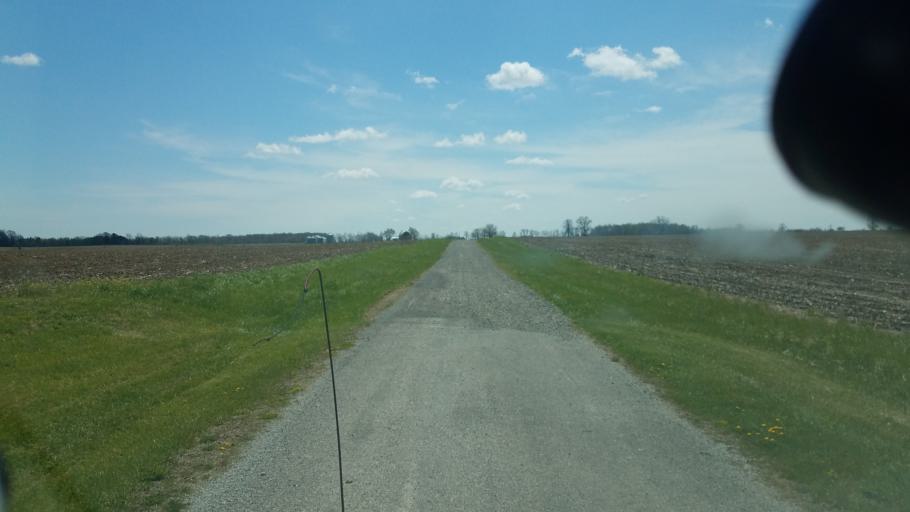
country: US
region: Ohio
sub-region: Union County
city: Richwood
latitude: 40.5224
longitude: -83.3610
